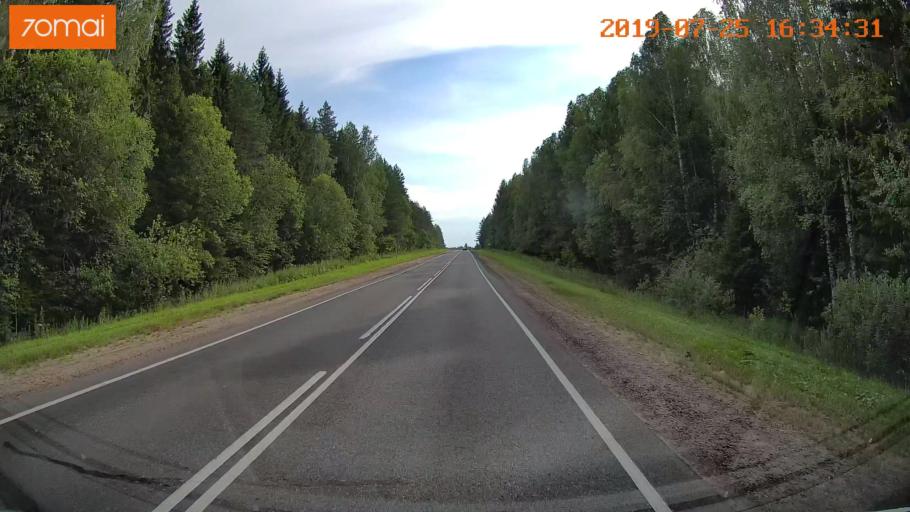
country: RU
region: Ivanovo
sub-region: Privolzhskiy Rayon
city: Ples
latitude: 57.4159
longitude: 41.4357
